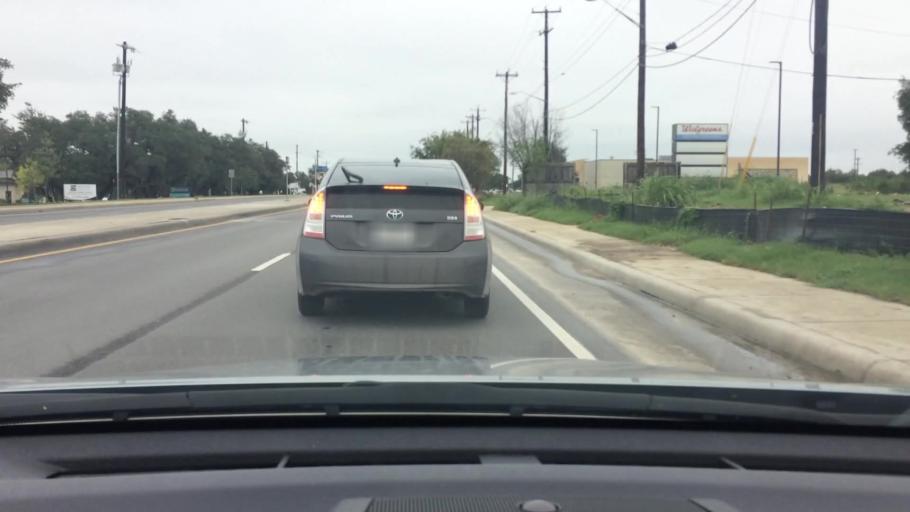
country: US
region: Texas
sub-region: Bexar County
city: Helotes
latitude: 29.5038
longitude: -98.7302
